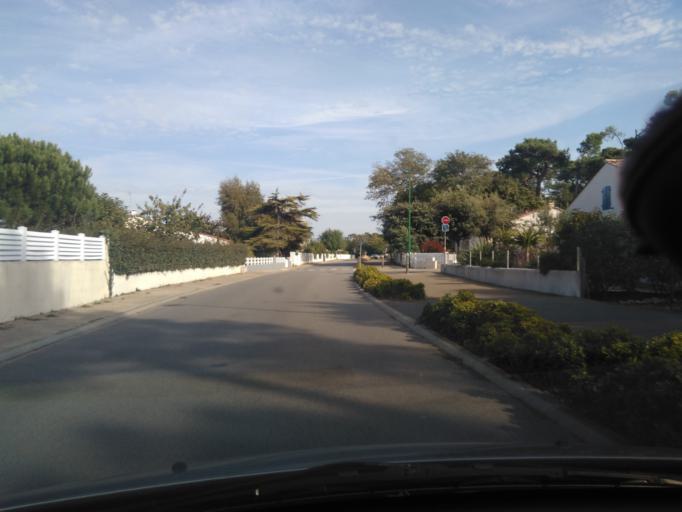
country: FR
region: Pays de la Loire
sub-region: Departement de la Vendee
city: Jard-sur-Mer
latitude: 46.4193
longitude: -1.5942
